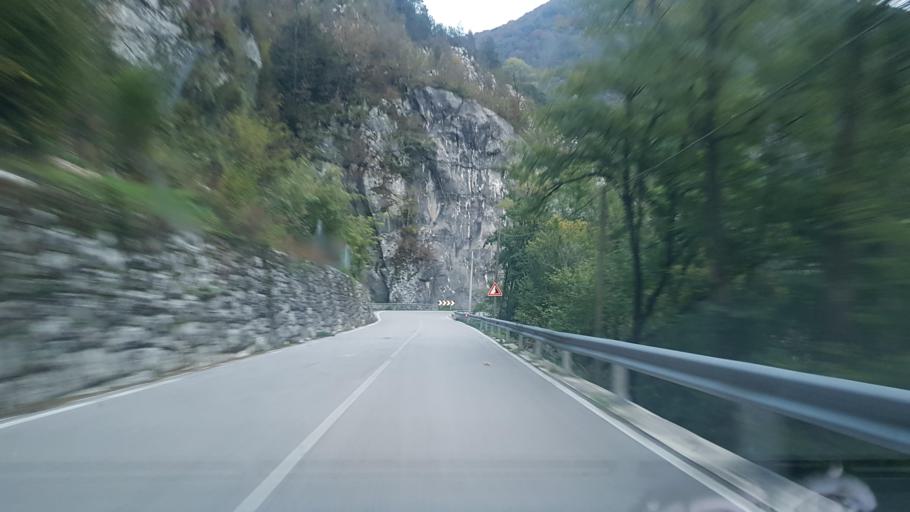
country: IT
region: Friuli Venezia Giulia
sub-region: Provincia di Pordenone
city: Anduins
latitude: 46.2696
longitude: 12.9521
